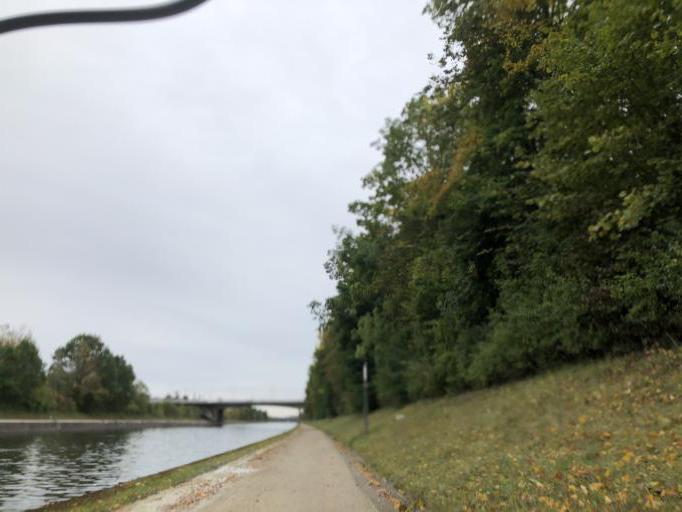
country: DE
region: Bavaria
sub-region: Regierungsbezirk Mittelfranken
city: Zirndorf
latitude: 49.4691
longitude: 10.9509
